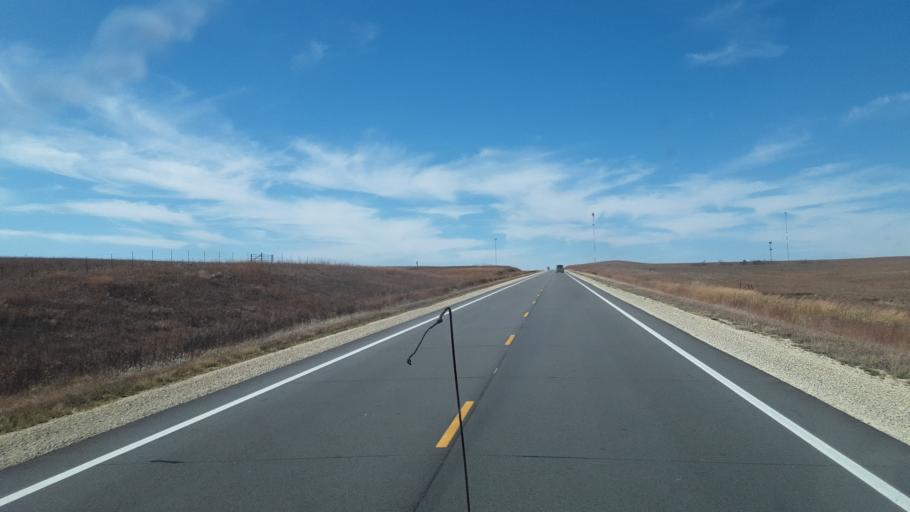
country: US
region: Kansas
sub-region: Chase County
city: Cottonwood Falls
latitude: 38.3627
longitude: -96.7205
